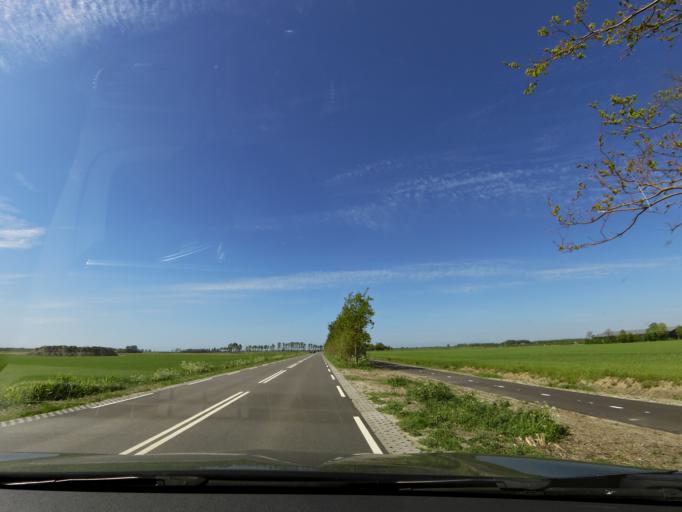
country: NL
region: Zeeland
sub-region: Schouwen-Duiveland
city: Bruinisse
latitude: 51.6595
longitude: 3.9909
